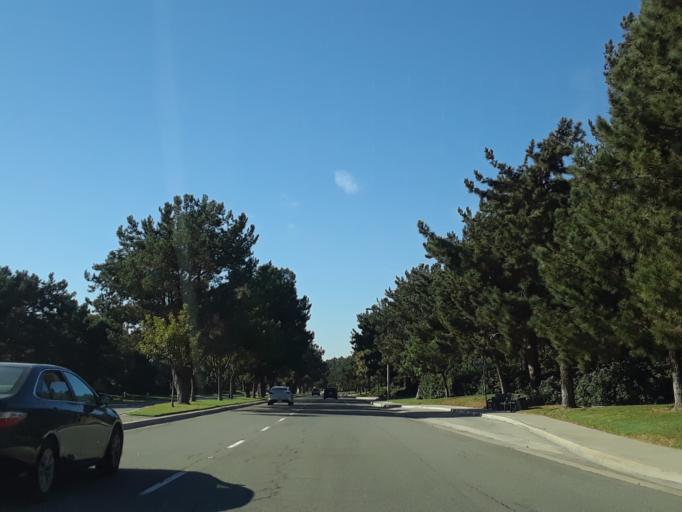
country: US
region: California
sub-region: Orange County
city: Irvine
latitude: 33.6765
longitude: -117.8172
